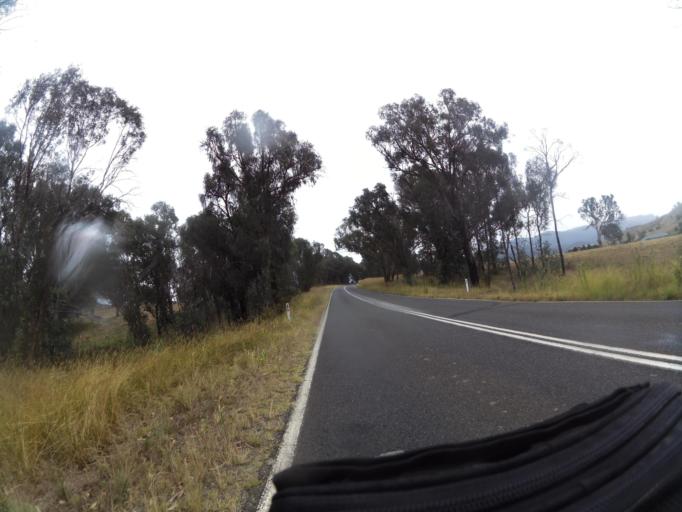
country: AU
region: New South Wales
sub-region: Greater Hume Shire
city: Holbrook
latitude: -36.2079
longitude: 147.8019
